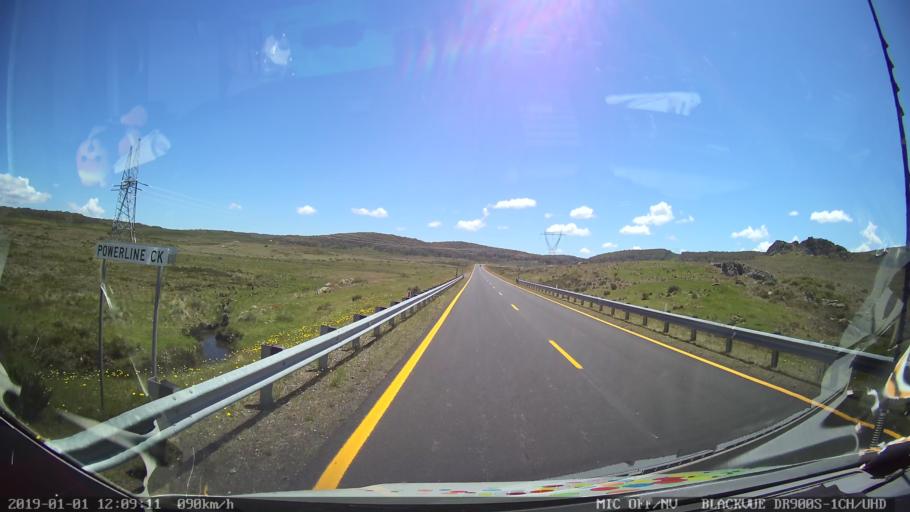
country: AU
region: New South Wales
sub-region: Tumut Shire
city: Tumut
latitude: -35.8105
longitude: 148.4962
